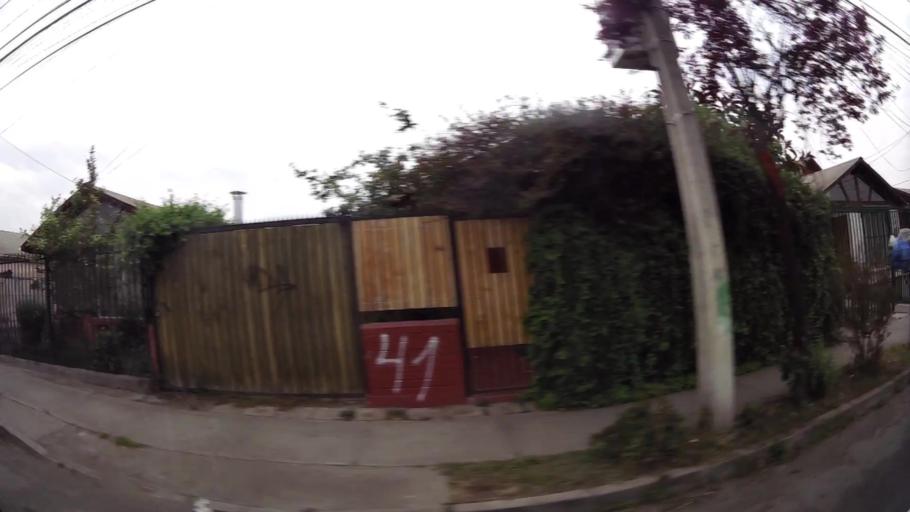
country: CL
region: Santiago Metropolitan
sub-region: Provincia de Santiago
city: Lo Prado
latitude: -33.4876
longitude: -70.7359
